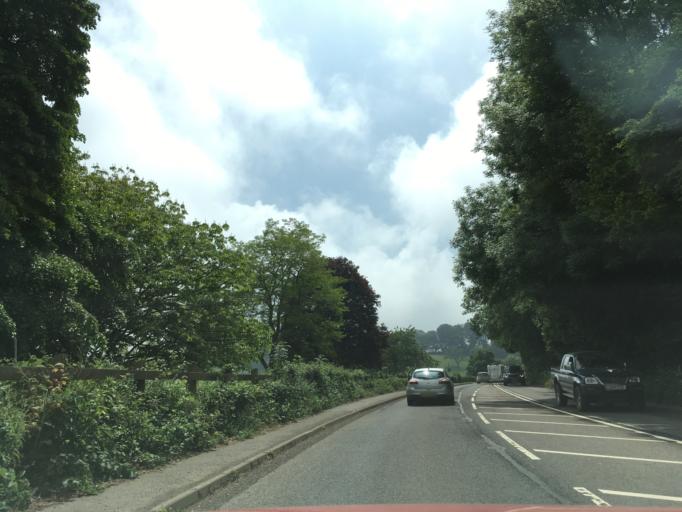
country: GB
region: England
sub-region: Devon
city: Totnes
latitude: 50.4268
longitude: -3.6903
